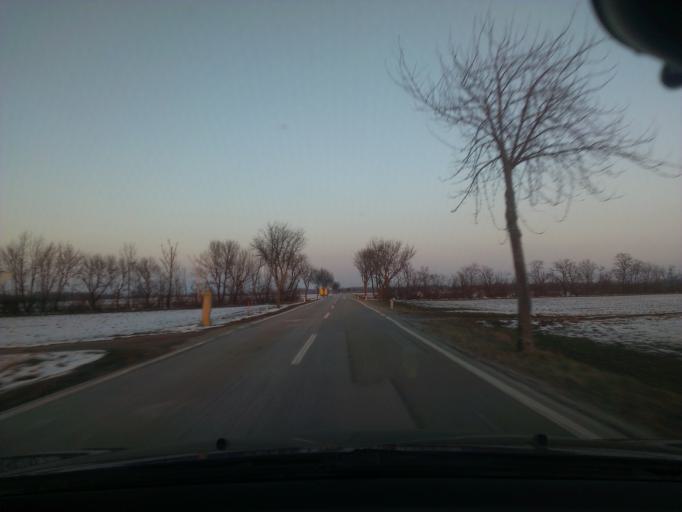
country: AT
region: Lower Austria
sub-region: Politischer Bezirk Baden
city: Reisenberg
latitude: 48.0001
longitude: 16.5455
